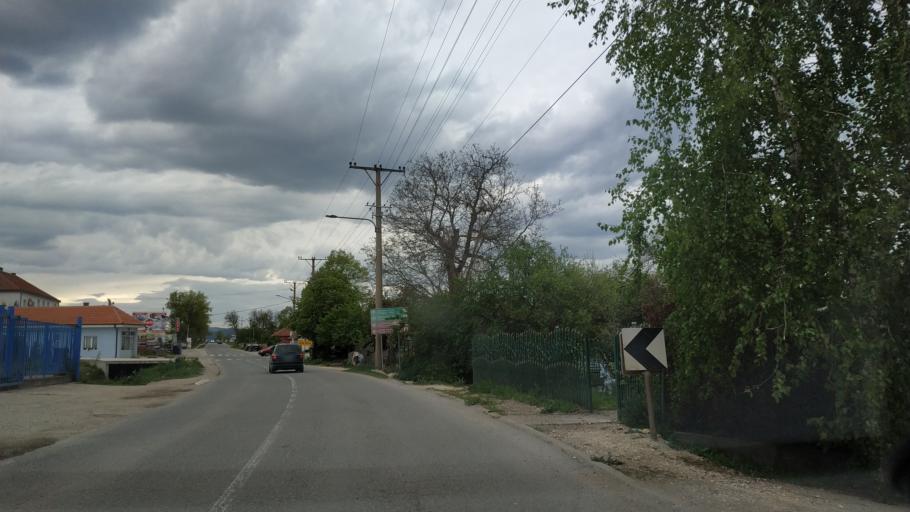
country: RS
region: Central Serbia
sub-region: Zajecarski Okrug
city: Soko Banja
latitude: 43.6503
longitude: 21.8575
